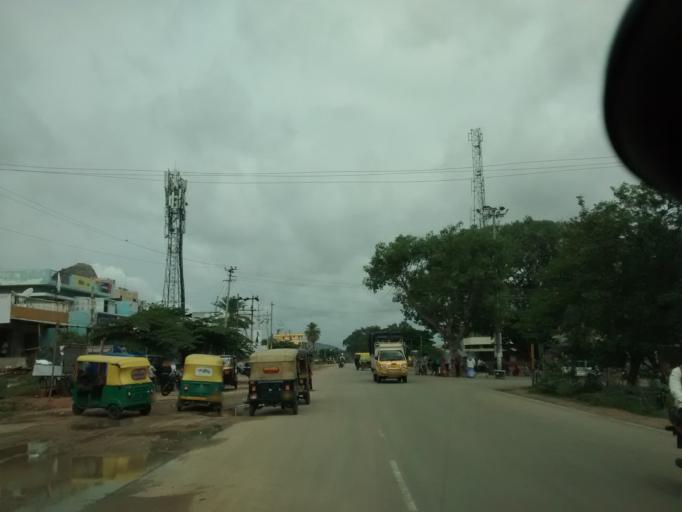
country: IN
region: Karnataka
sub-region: Tumkur
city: Madhugiri
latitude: 13.6622
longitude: 77.2278
